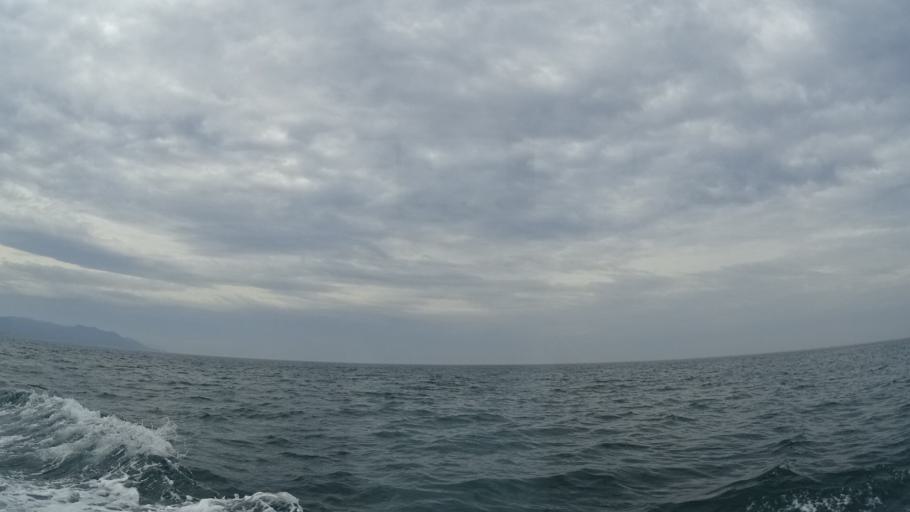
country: JP
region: Fukui
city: Mikuni
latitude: 36.2480
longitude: 136.1182
